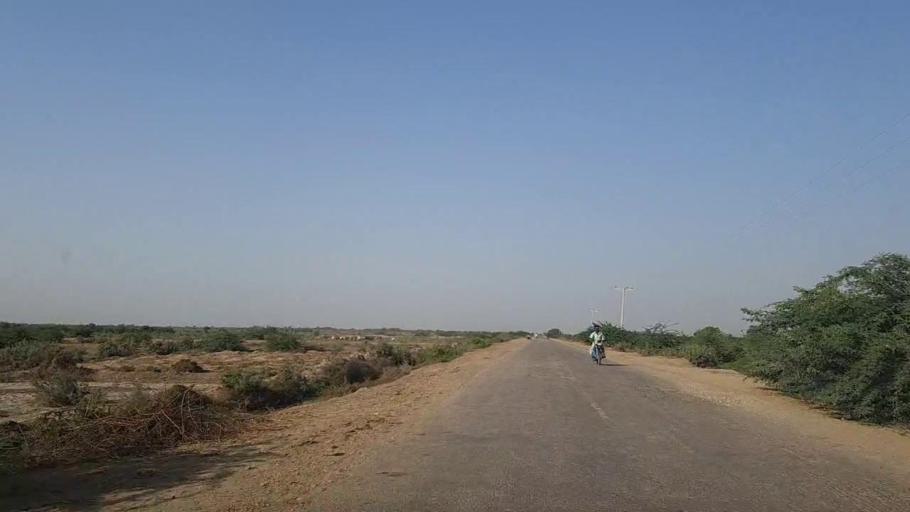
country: PK
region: Sindh
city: Mirpur Batoro
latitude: 24.6054
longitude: 68.4019
